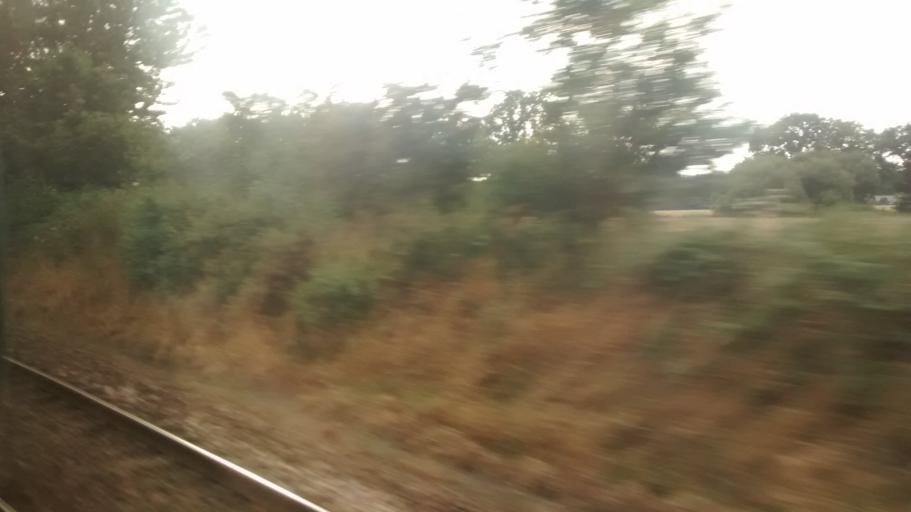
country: FR
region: Brittany
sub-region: Departement d'Ille-et-Vilaine
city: Cesson-Sevigne
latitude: 48.1192
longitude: -1.5778
